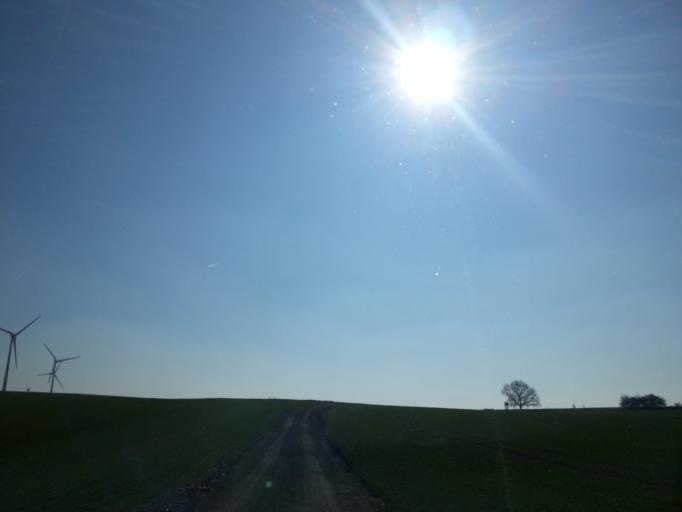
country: DE
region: Saxony
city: Niederschona
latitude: 50.9240
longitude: 13.4006
